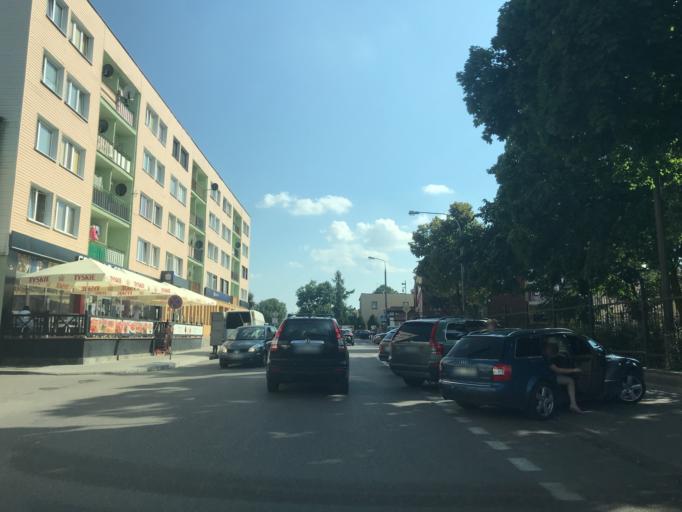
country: PL
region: Masovian Voivodeship
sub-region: Powiat mlawski
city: Mlawa
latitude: 53.1123
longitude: 20.3794
